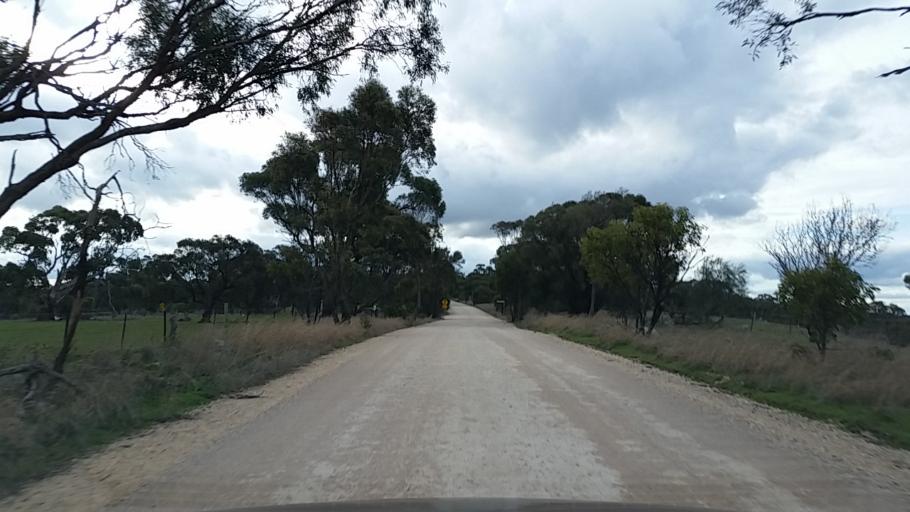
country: AU
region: South Australia
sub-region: Mount Barker
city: Callington
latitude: -35.0012
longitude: 139.0603
